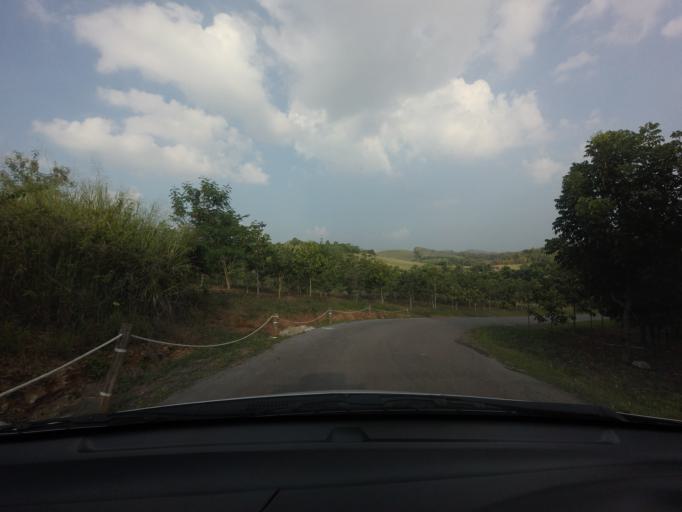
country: TH
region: Nakhon Ratchasima
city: Pak Chong
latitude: 14.5151
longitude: 101.5674
